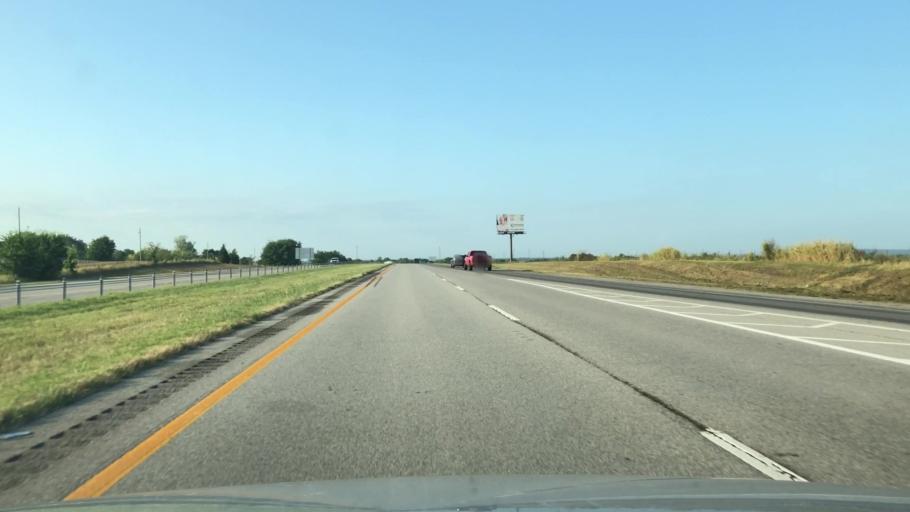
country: US
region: Oklahoma
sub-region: Osage County
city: Skiatook
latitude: 36.3626
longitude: -95.9208
